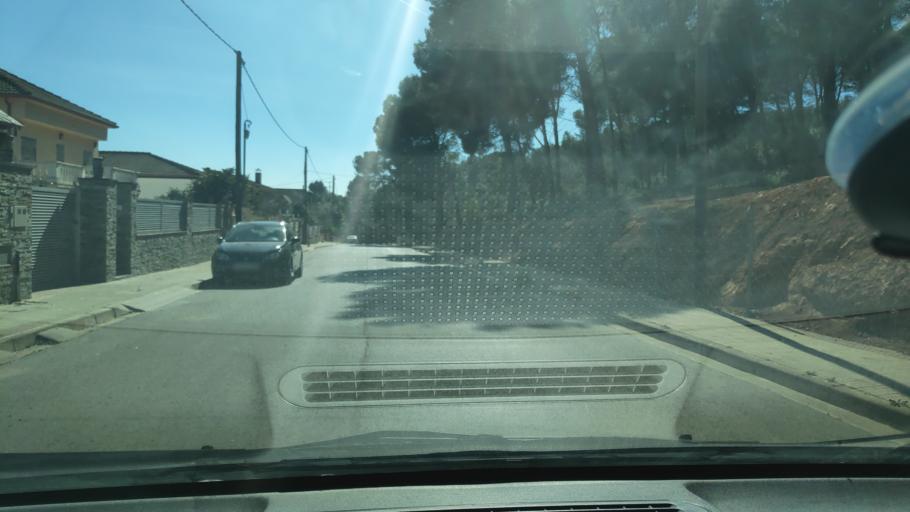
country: ES
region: Catalonia
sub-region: Provincia de Barcelona
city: Rubi
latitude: 41.5236
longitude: 2.0321
